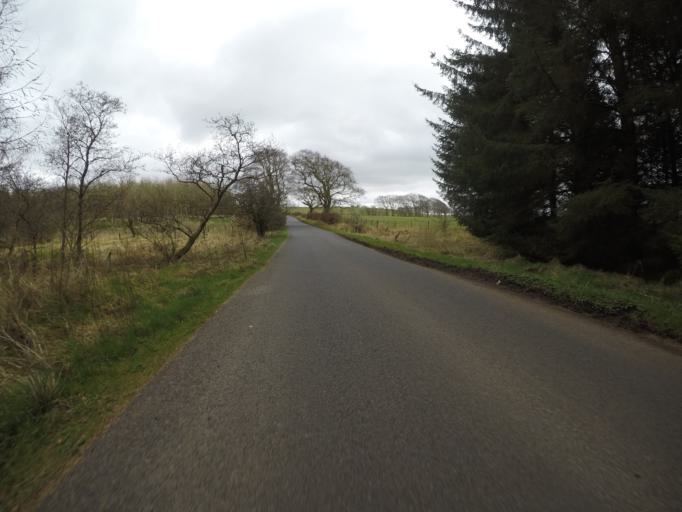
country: GB
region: Scotland
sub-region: East Ayrshire
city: Stewarton
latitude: 55.6803
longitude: -4.4515
